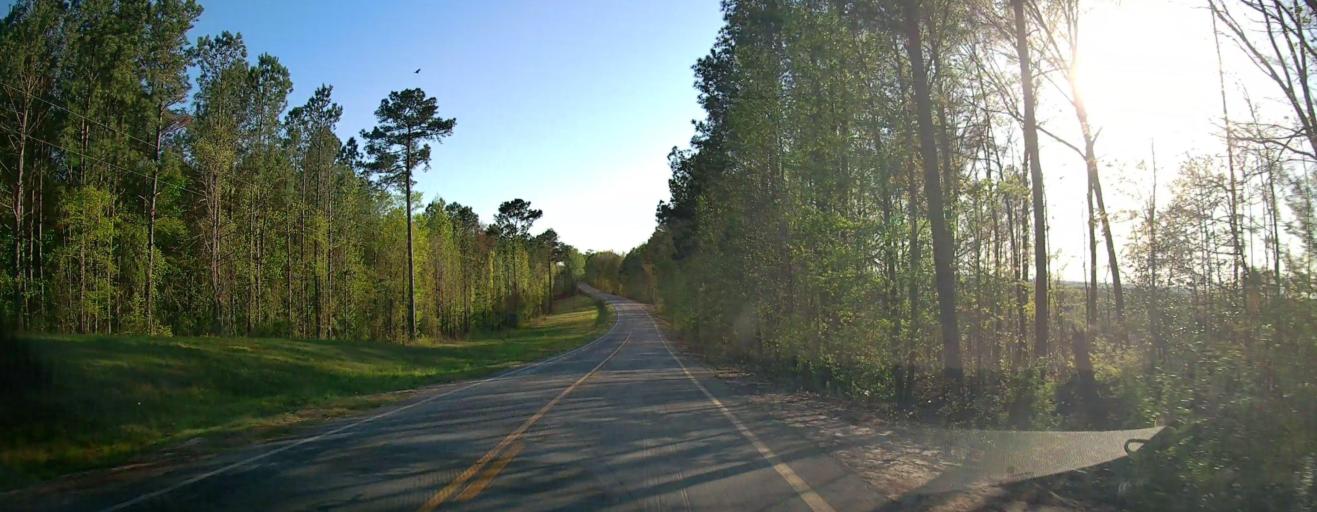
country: US
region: Georgia
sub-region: Wilkinson County
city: Irwinton
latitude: 32.8437
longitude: -83.0646
